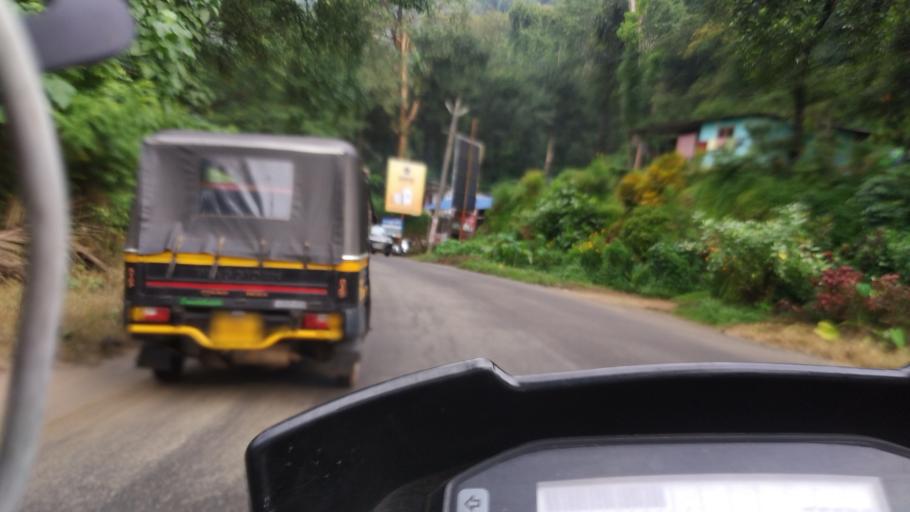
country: IN
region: Kerala
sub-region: Idukki
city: Kuttampuzha
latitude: 10.0491
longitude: 76.7576
